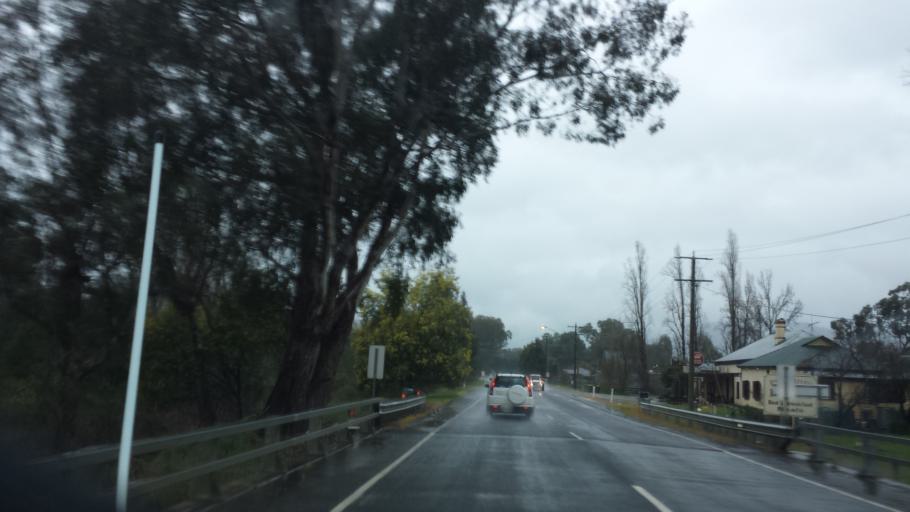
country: AU
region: Victoria
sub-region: Alpine
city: Mount Beauty
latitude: -36.5859
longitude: 146.7586
